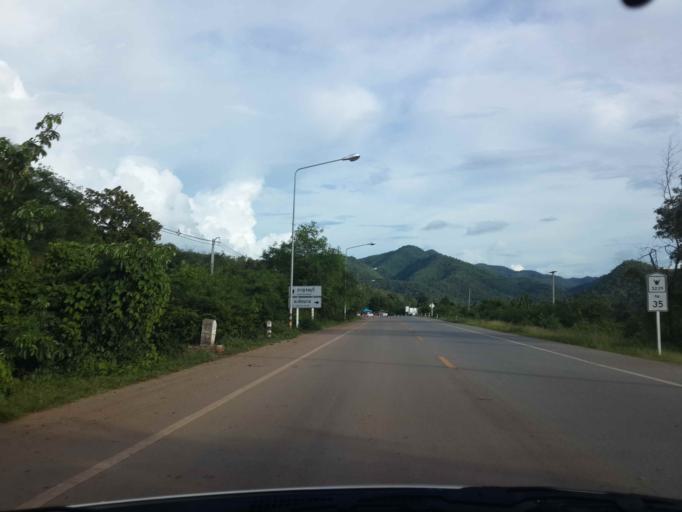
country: TH
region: Kanchanaburi
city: Sai Yok
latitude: 13.8840
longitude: 99.1705
